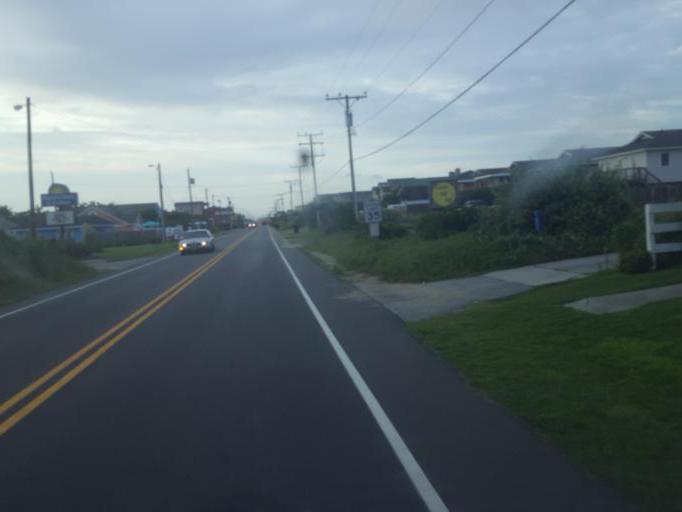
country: US
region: North Carolina
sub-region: Dare County
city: Kill Devil Hills
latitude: 36.0352
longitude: -75.6700
